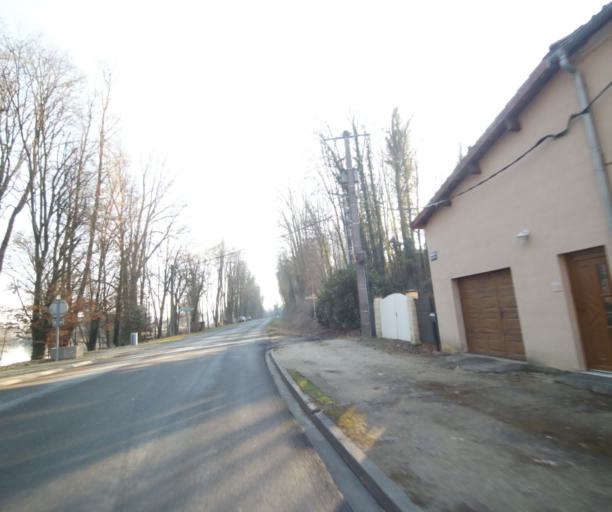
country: FR
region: Champagne-Ardenne
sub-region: Departement de la Haute-Marne
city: Bienville
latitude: 48.5811
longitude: 5.0397
